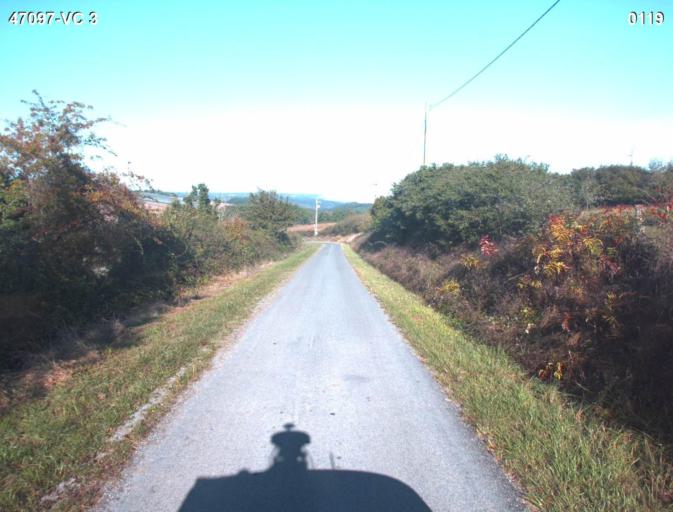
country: FR
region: Aquitaine
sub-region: Departement du Lot-et-Garonne
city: Vianne
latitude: 44.1958
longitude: 0.3626
